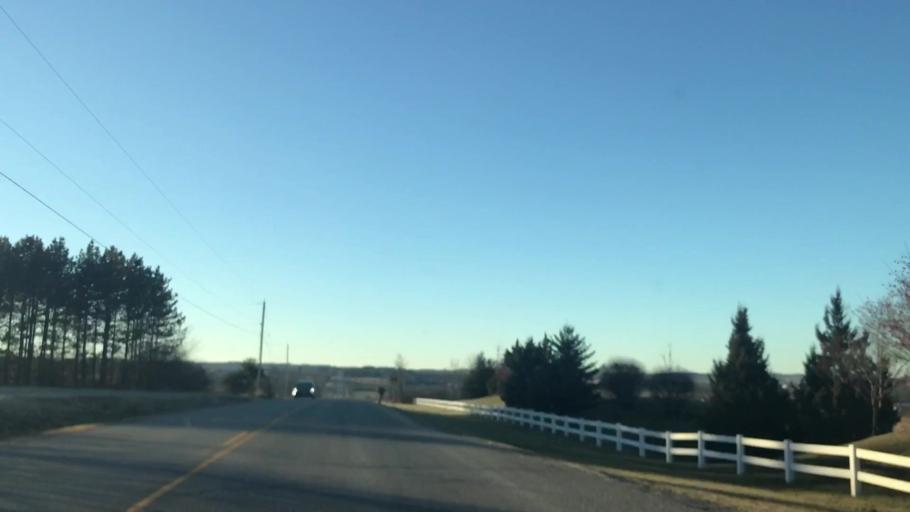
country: US
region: Wisconsin
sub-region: Washington County
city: Jackson
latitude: 43.2949
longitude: -88.1527
